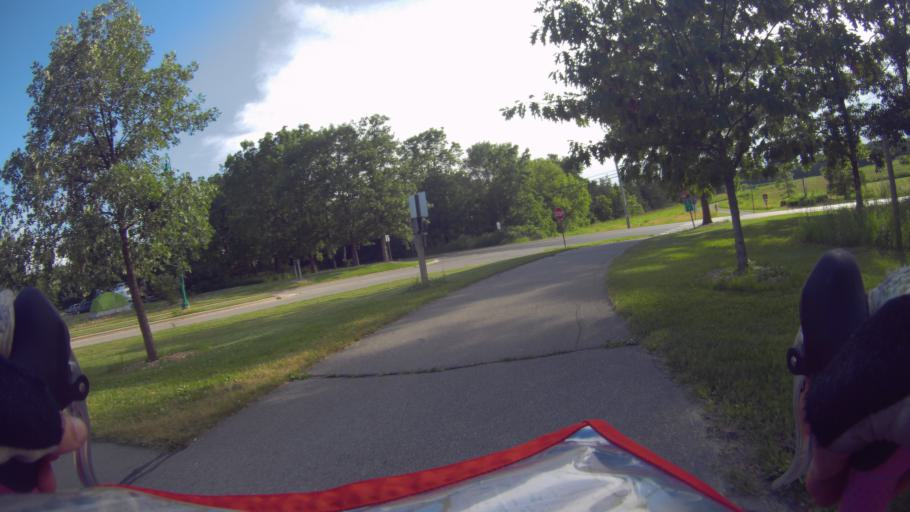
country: US
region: Wisconsin
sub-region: Dane County
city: Monona
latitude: 43.0271
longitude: -89.3453
